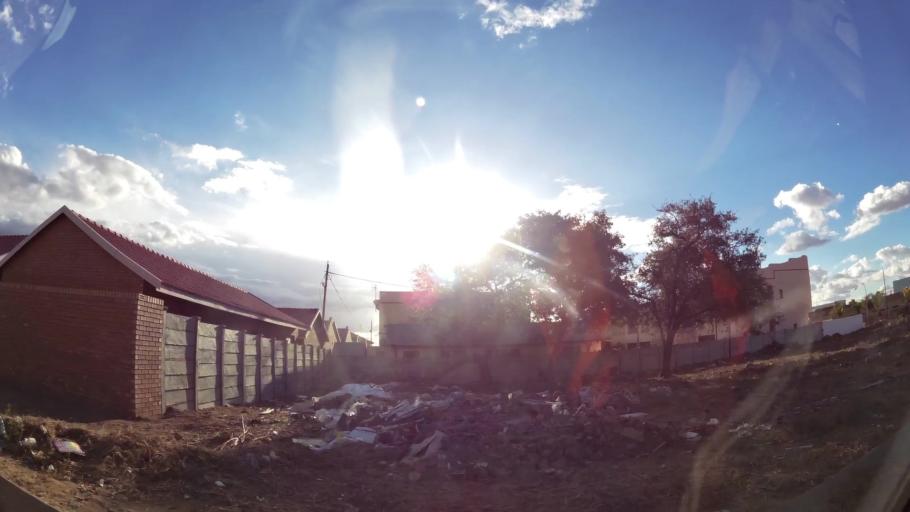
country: ZA
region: Limpopo
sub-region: Capricorn District Municipality
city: Polokwane
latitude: -23.9179
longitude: 29.4311
